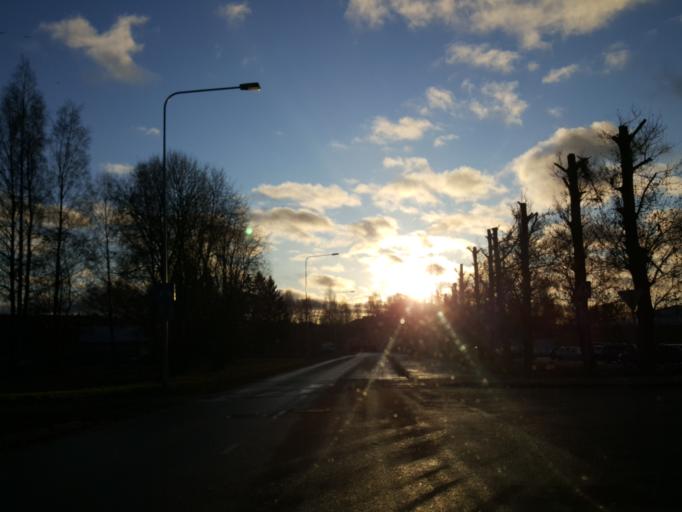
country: FI
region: Uusimaa
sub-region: Helsinki
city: Lohja
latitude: 60.2528
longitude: 24.0570
